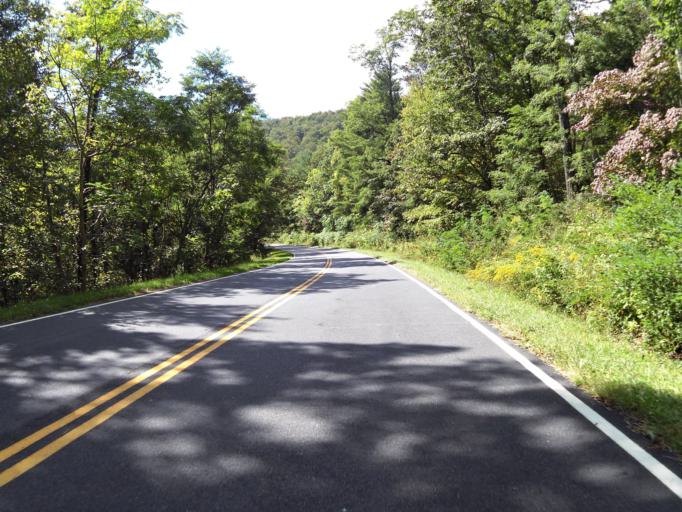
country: US
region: Virginia
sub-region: Rappahannock County
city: Washington
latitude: 38.7367
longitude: -78.3157
